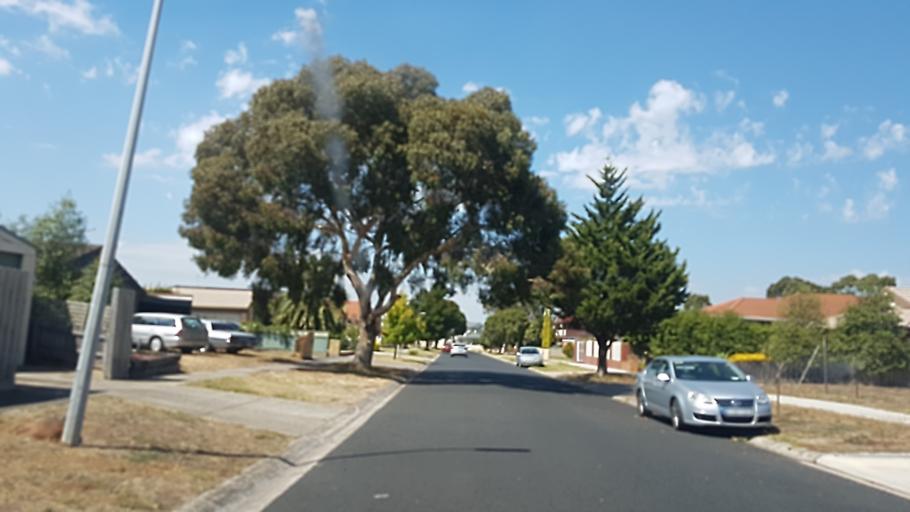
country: AU
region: Victoria
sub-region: Brimbank
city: Keilor Lodge
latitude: -37.6999
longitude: 144.7969
